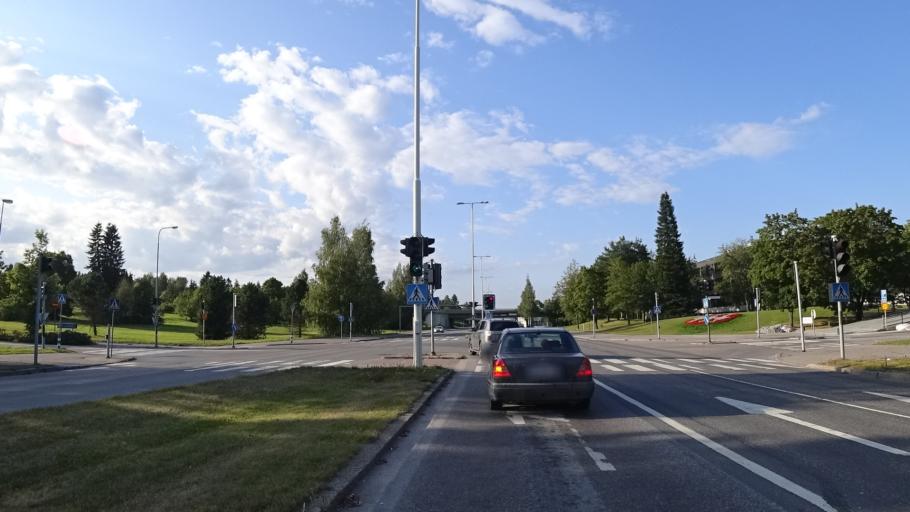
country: FI
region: South Karelia
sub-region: Imatra
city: Imatra
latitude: 61.1919
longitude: 28.7767
